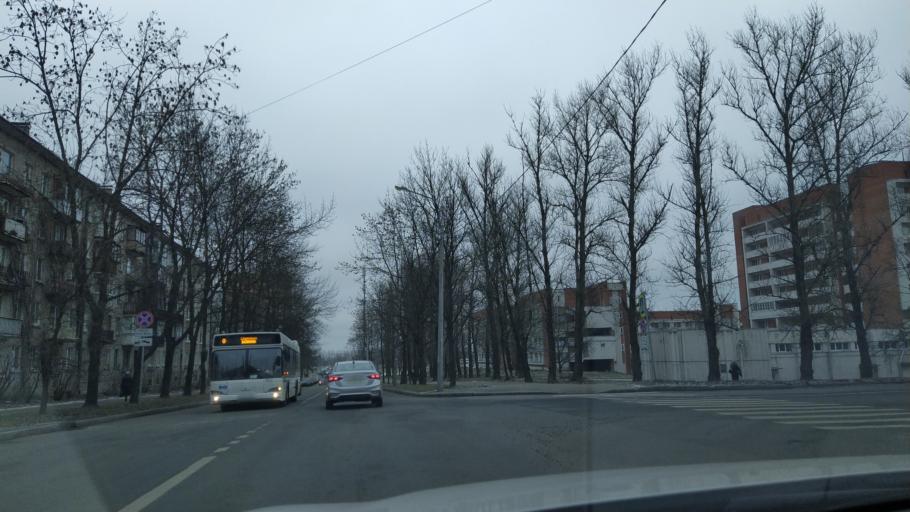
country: RU
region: St.-Petersburg
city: Pushkin
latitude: 59.7282
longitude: 30.4195
